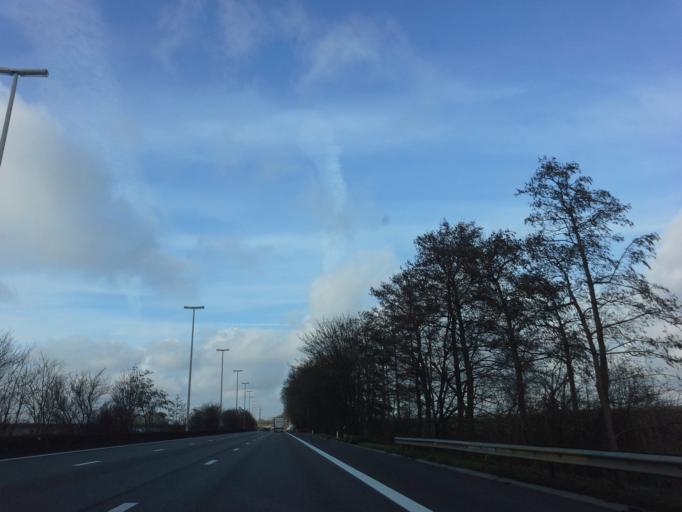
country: BE
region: Flanders
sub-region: Provincie Vlaams-Brabant
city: Boutersem
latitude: 50.8132
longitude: 4.8584
